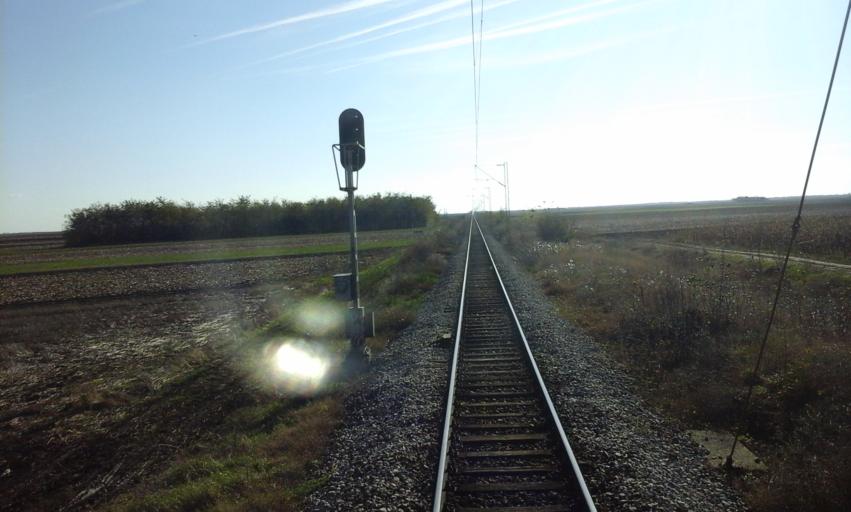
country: RS
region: Autonomna Pokrajina Vojvodina
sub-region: Severnobacki Okrug
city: Backa Topola
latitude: 45.9297
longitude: 19.6667
